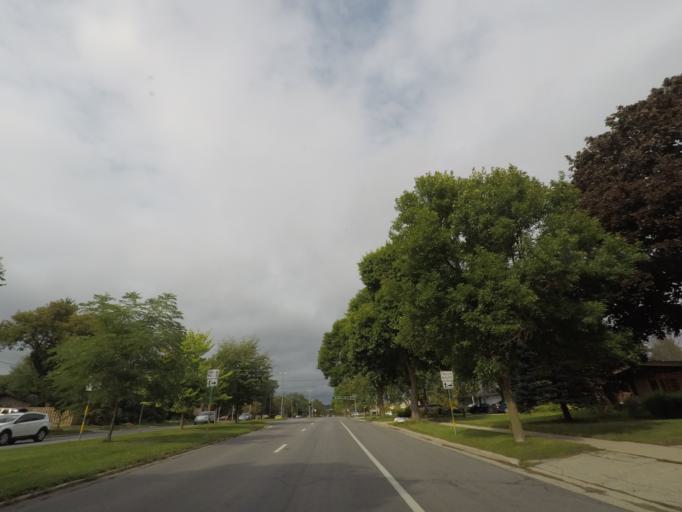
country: US
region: Wisconsin
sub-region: Dane County
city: Shorewood Hills
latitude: 43.0320
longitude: -89.4756
